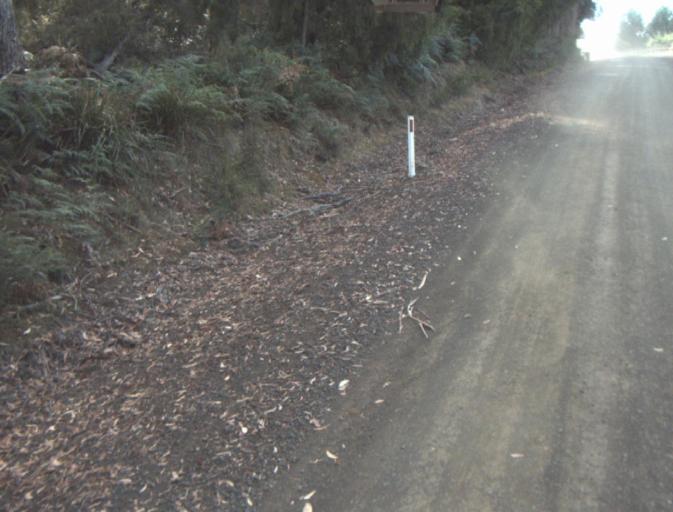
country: AU
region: Tasmania
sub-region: Launceston
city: Mayfield
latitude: -41.2716
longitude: 147.1718
